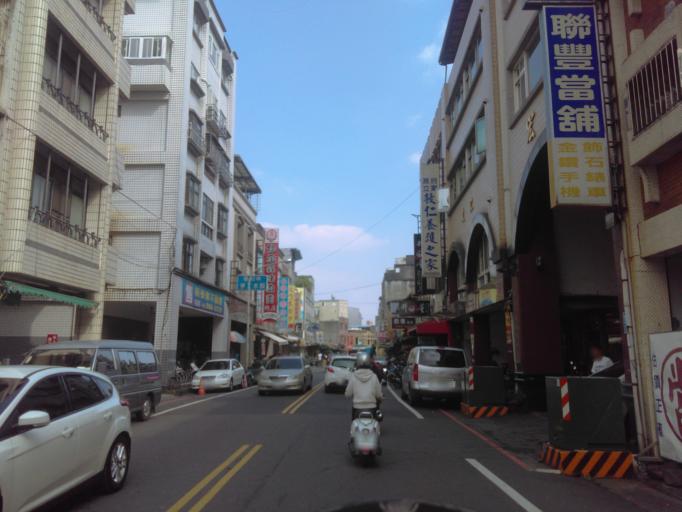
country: TW
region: Taiwan
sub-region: Yilan
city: Yilan
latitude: 24.7605
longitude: 121.7517
